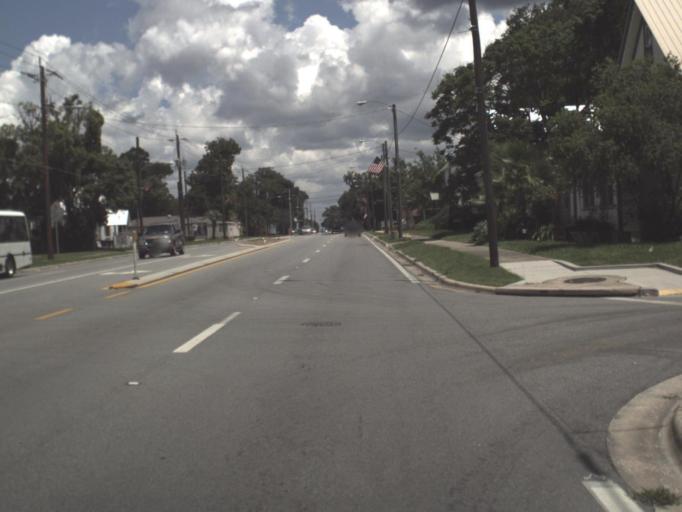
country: US
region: Florida
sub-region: Putnam County
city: Crescent City
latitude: 29.4326
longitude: -81.5104
